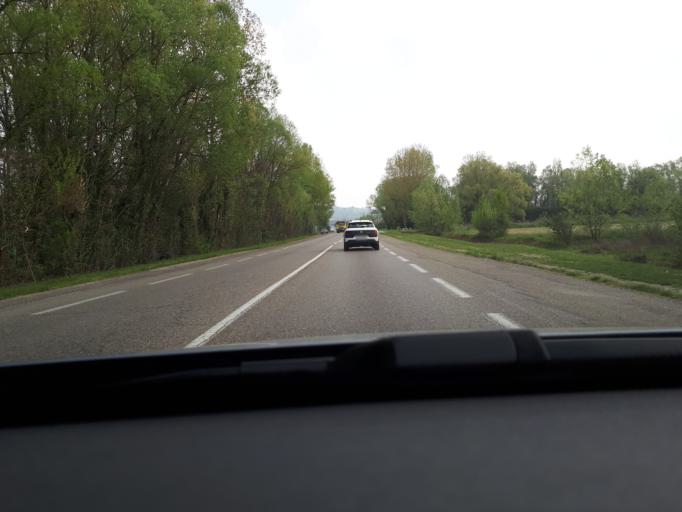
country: FR
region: Rhone-Alpes
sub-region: Departement de l'Isere
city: Bourgoin-Jallieu
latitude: 45.5905
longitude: 5.2587
